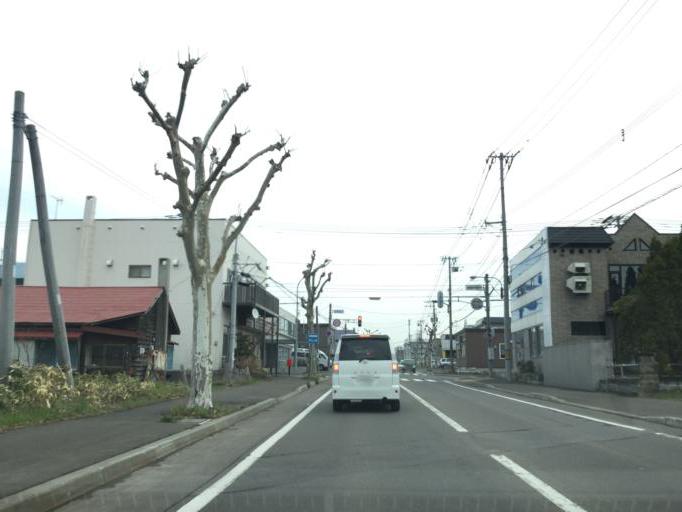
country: JP
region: Hokkaido
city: Iwamizawa
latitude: 43.2066
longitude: 141.7770
